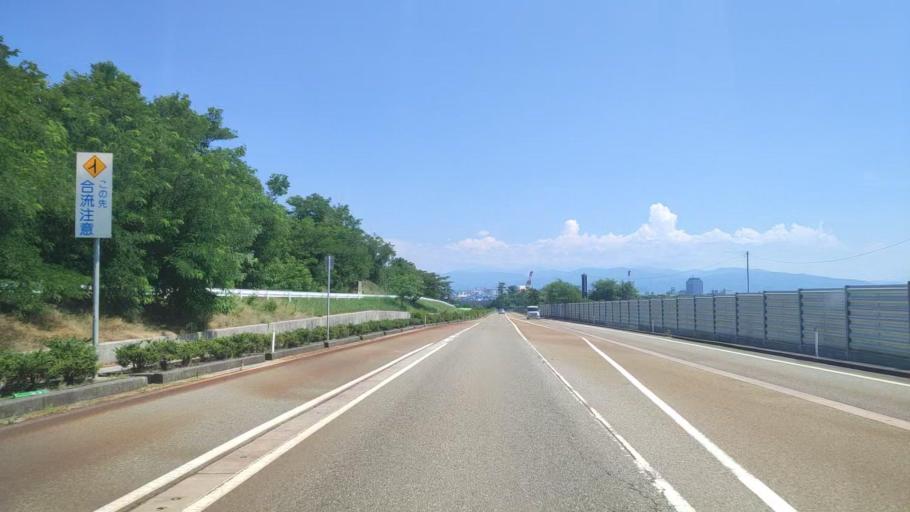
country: JP
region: Ishikawa
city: Kanazawa-shi
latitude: 36.6232
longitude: 136.6168
